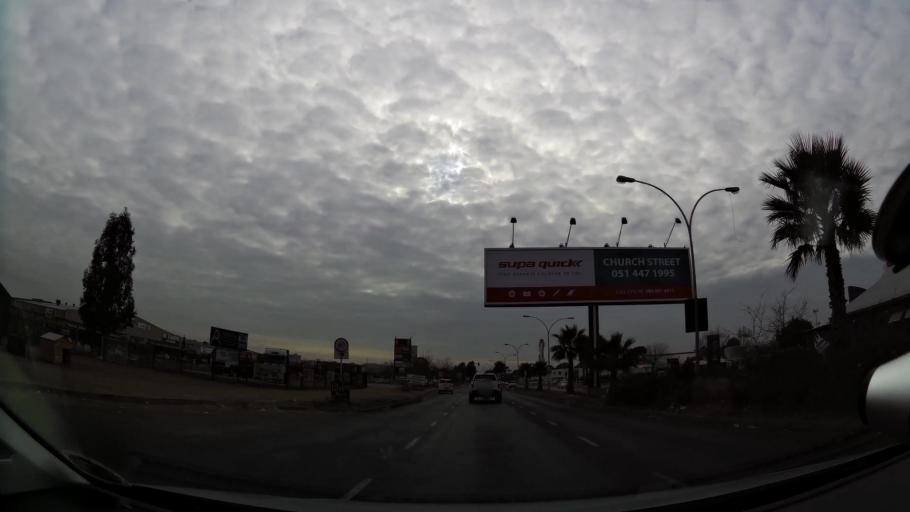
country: ZA
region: Orange Free State
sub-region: Mangaung Metropolitan Municipality
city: Bloemfontein
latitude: -29.1362
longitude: 26.2035
